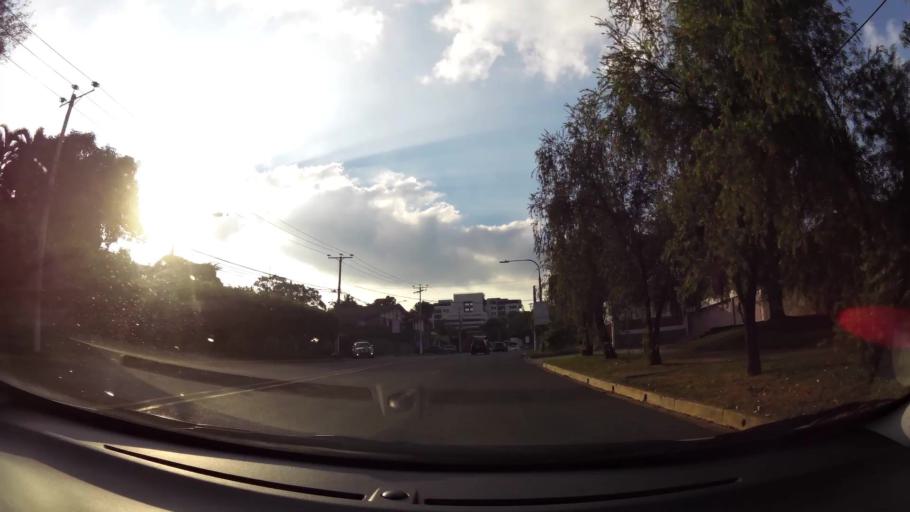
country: SV
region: La Libertad
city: Antiguo Cuscatlan
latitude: 13.6890
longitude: -89.2423
